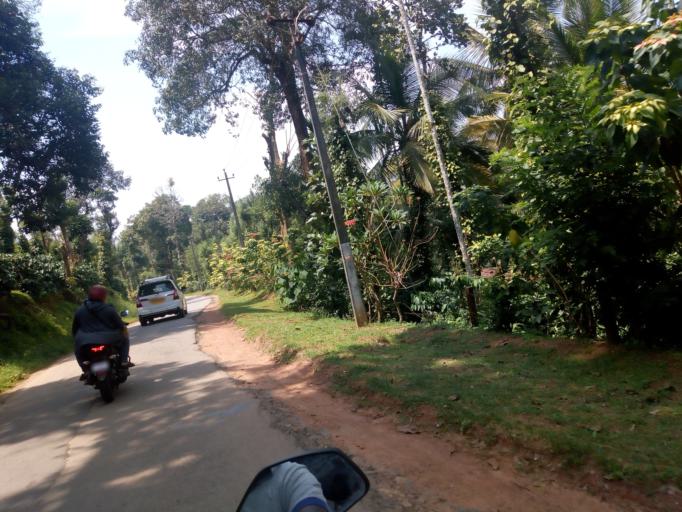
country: IN
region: Karnataka
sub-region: Kodagu
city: Ponnampet
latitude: 12.0326
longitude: 75.9524
